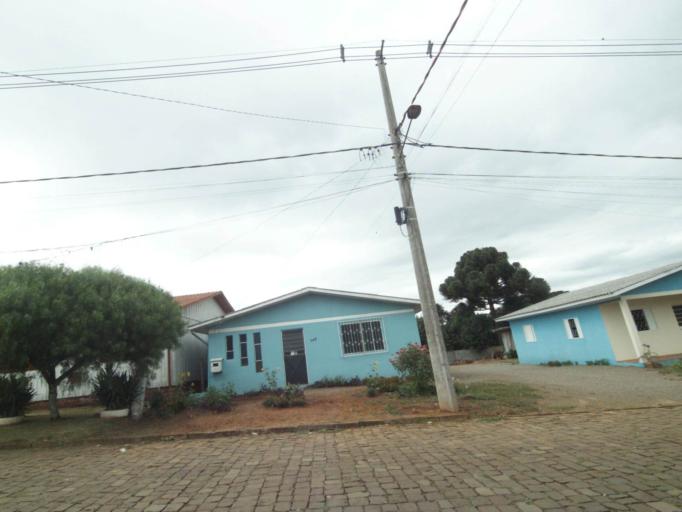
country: BR
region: Rio Grande do Sul
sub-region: Lagoa Vermelha
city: Lagoa Vermelha
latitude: -28.2140
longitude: -51.5055
